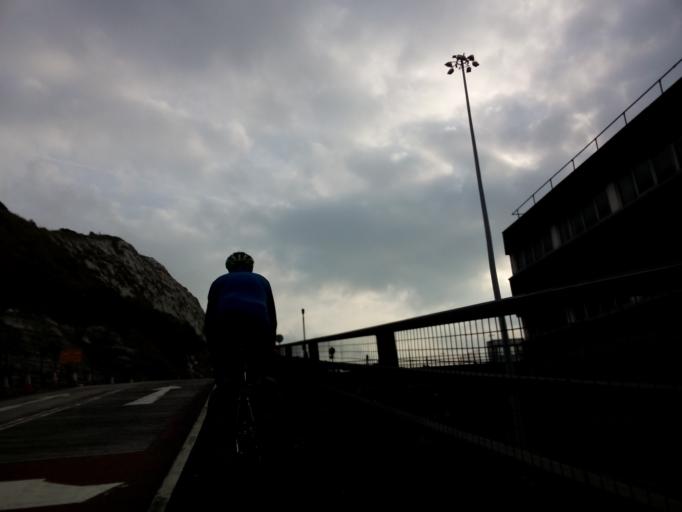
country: GB
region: England
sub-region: Kent
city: Dover
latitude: 51.1282
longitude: 1.3303
